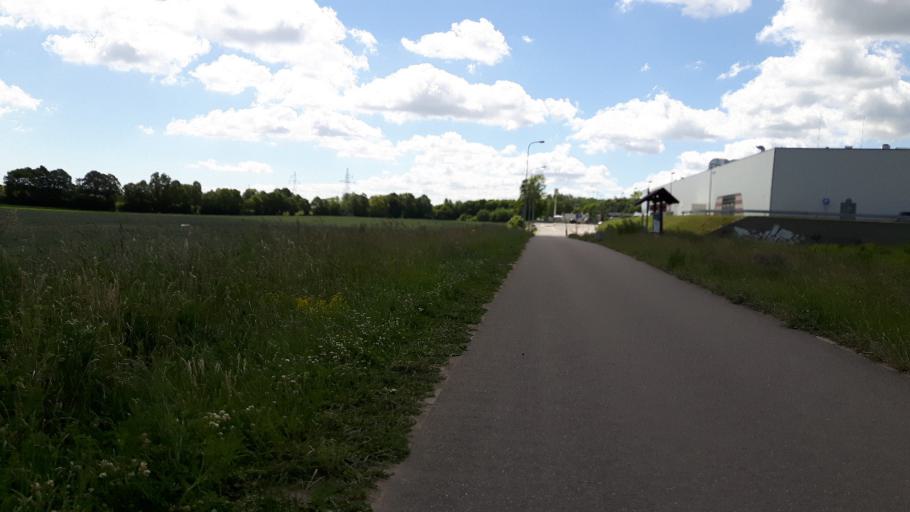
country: PL
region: Pomeranian Voivodeship
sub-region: Gdynia
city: Pogorze
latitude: 54.5669
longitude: 18.5045
